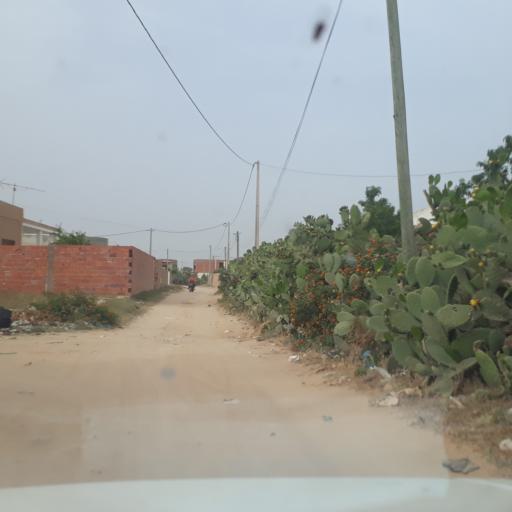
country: TN
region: Safaqis
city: Al Qarmadah
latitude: 34.8264
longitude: 10.7752
